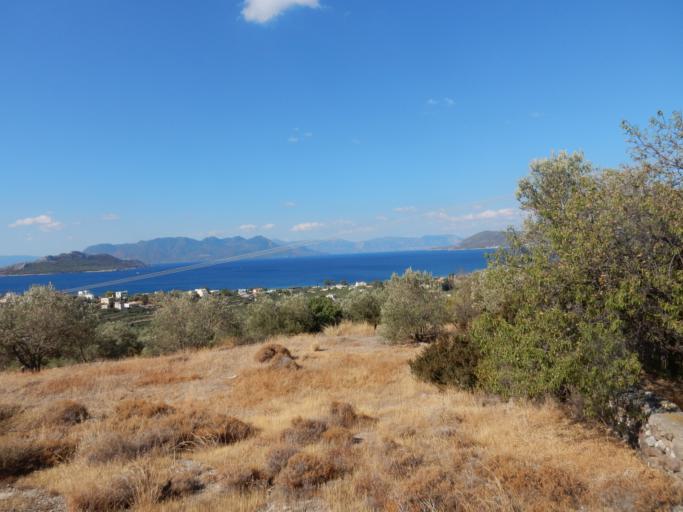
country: GR
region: Attica
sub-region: Nomos Piraios
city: Aegina
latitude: 37.7315
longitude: 23.4513
